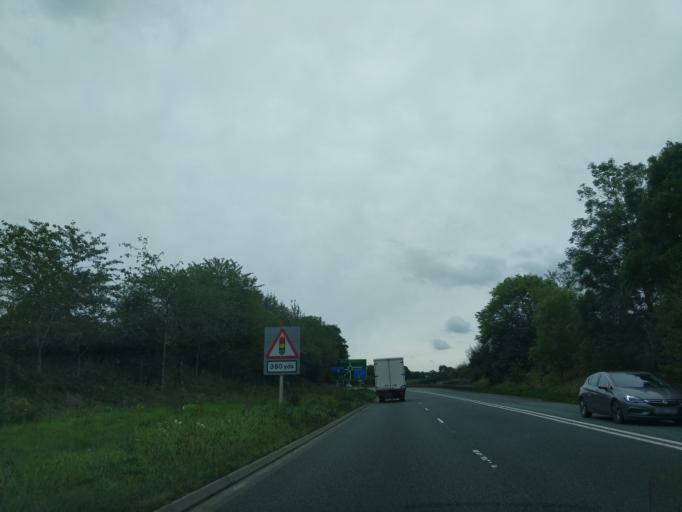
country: GB
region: England
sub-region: Cheshire East
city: Alsager
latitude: 53.0694
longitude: -2.3406
